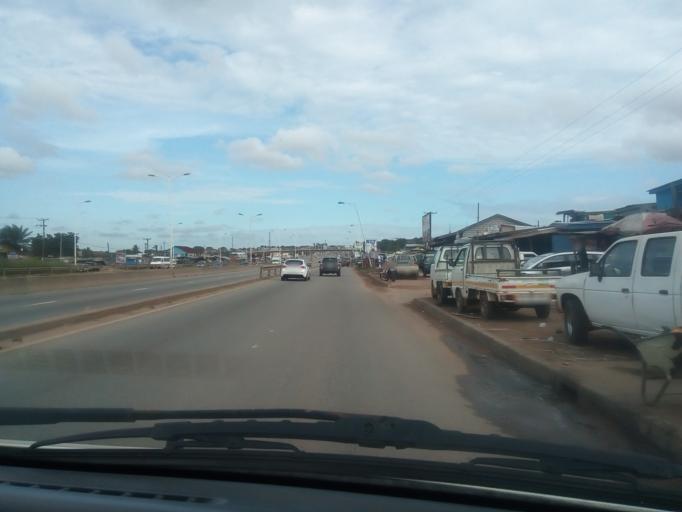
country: GH
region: Greater Accra
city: Dome
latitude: 5.6511
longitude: -0.2557
